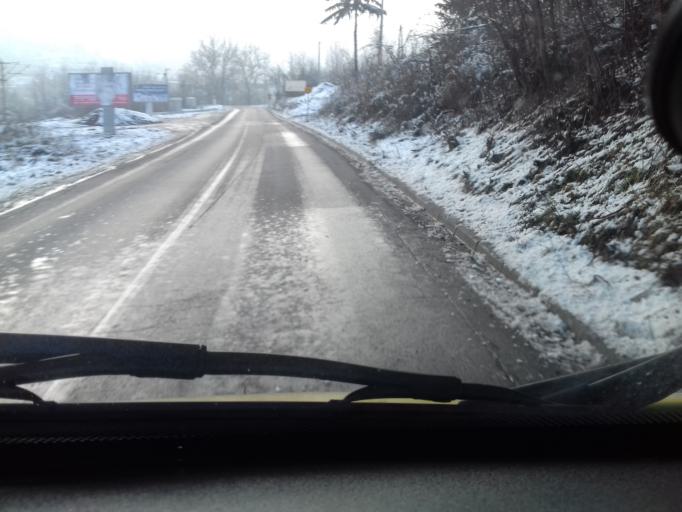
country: BA
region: Federation of Bosnia and Herzegovina
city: Visoko
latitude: 43.9936
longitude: 18.2028
